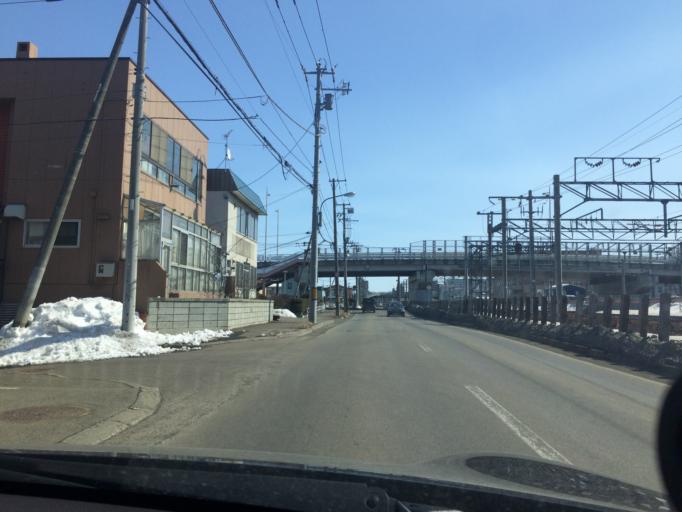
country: JP
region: Hokkaido
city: Sapporo
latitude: 43.0625
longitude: 141.4014
